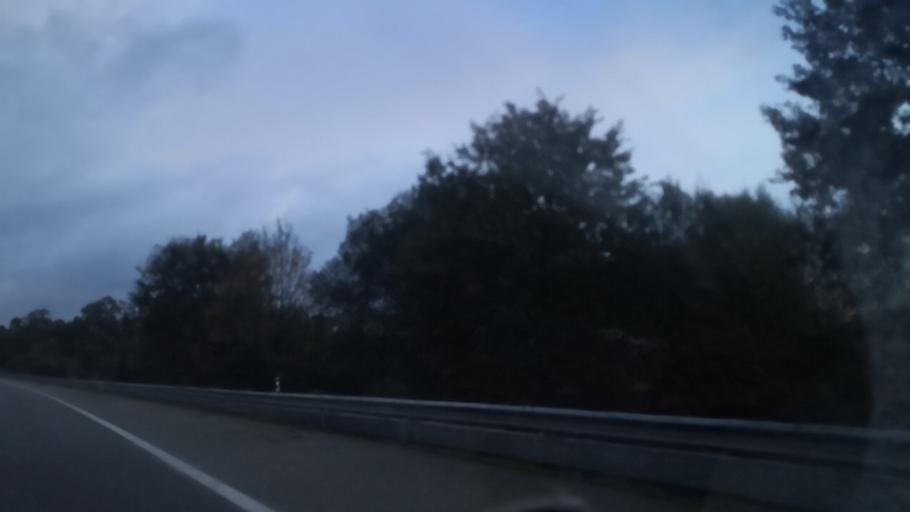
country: PT
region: Braga
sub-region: Vila Verde
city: Prado
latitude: 41.6583
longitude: -8.5483
